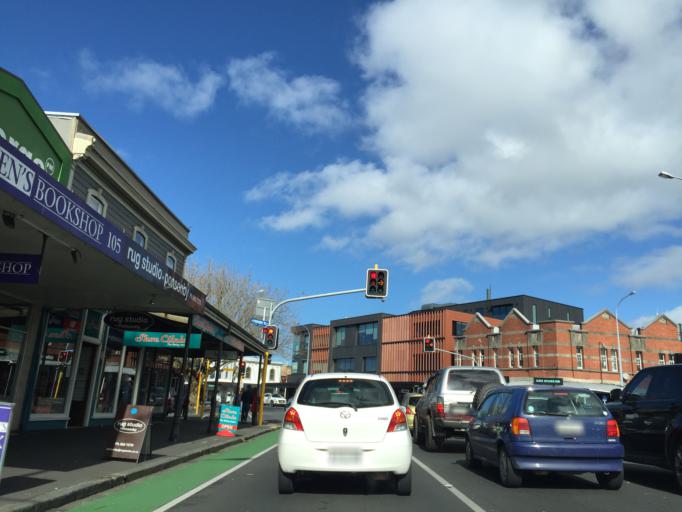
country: NZ
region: Auckland
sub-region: Auckland
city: Auckland
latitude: -36.8560
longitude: 174.7466
